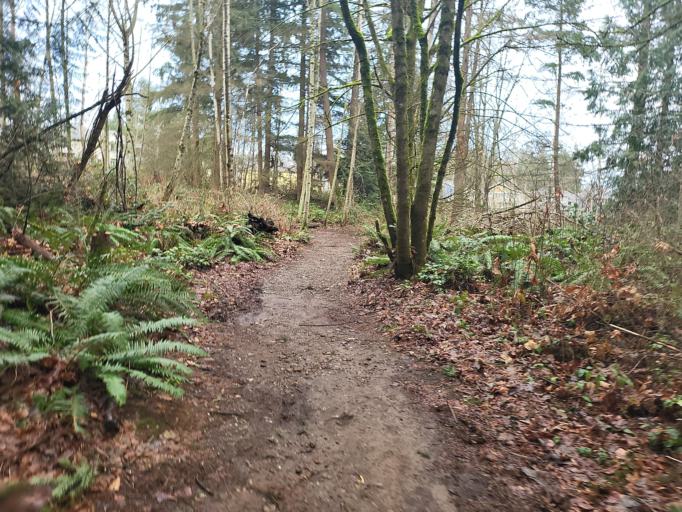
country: US
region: Washington
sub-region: King County
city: East Renton Highlands
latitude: 47.4805
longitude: -122.1385
